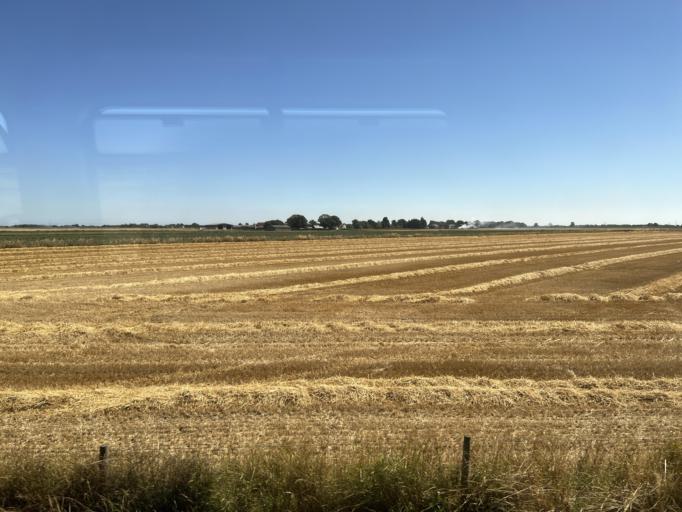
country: GB
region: England
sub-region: Lincolnshire
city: Spilsby
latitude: 53.0985
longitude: 0.1083
